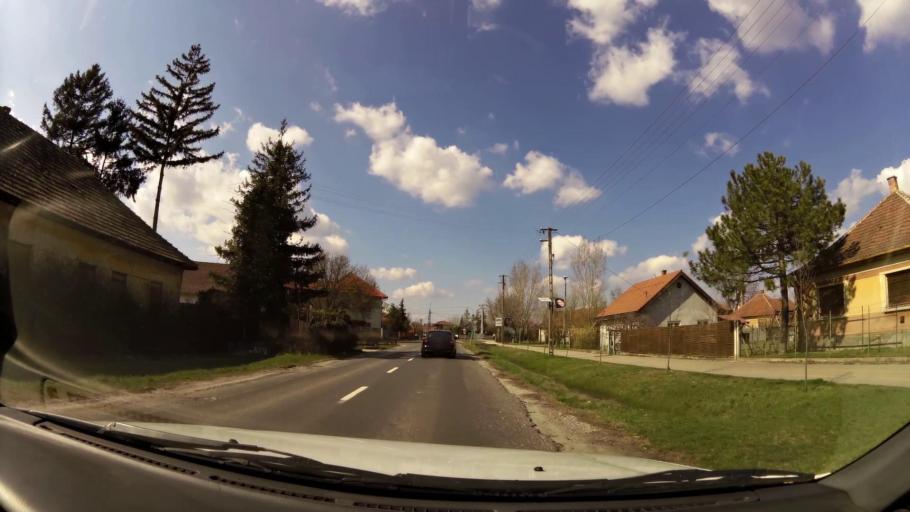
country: HU
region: Pest
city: Nagykata
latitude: 47.4075
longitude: 19.7458
